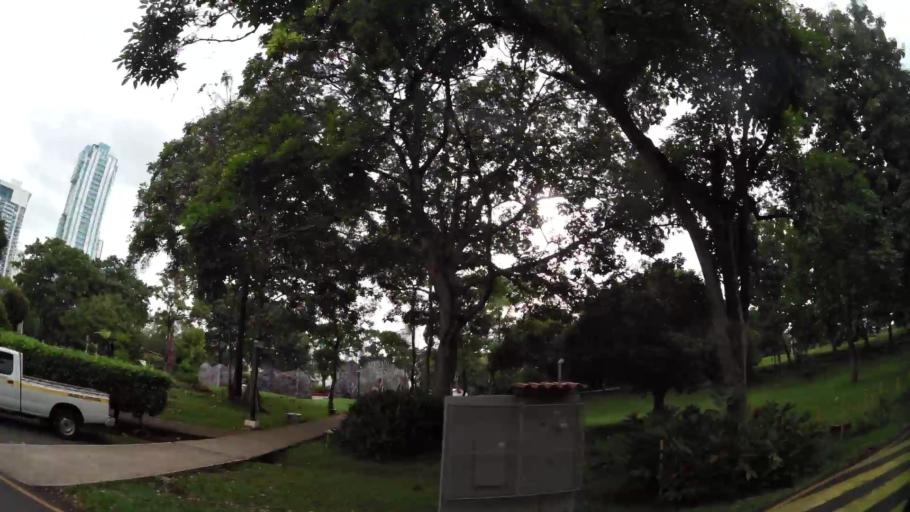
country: PA
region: Panama
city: Panama
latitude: 8.9984
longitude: -79.5070
